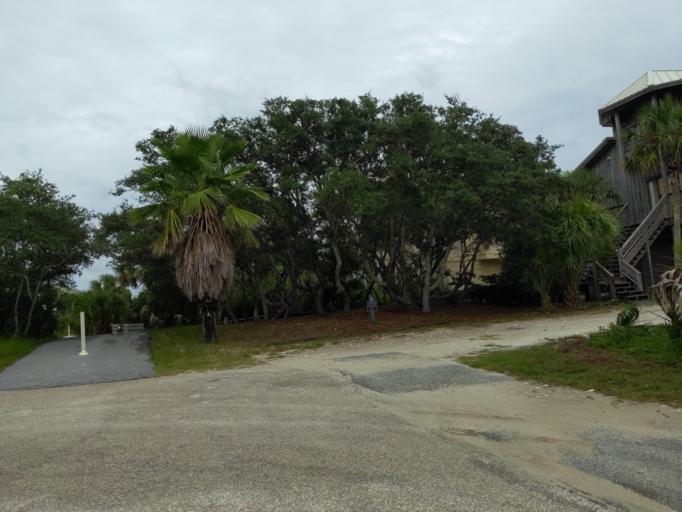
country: US
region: Florida
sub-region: Franklin County
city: Apalachicola
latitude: 29.6289
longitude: -84.9293
